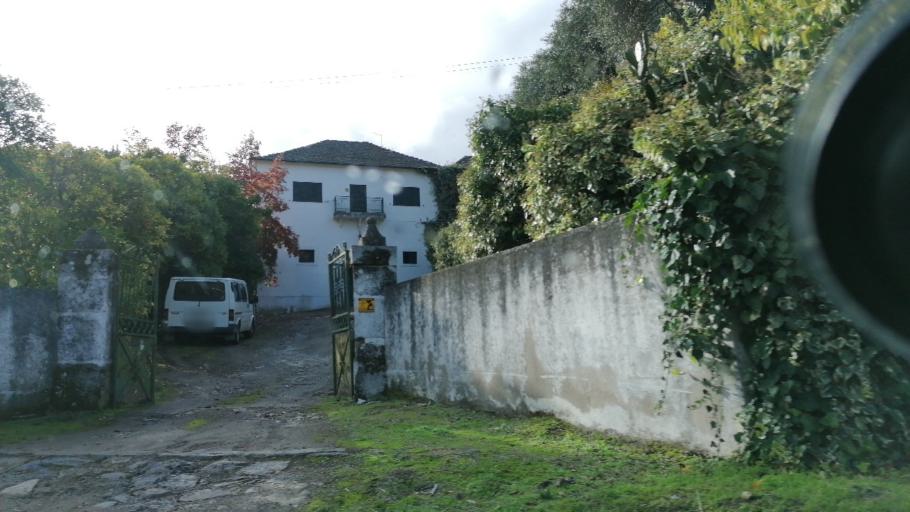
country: PT
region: Vila Real
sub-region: Peso da Regua
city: Peso da Regua
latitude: 41.1426
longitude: -7.7802
